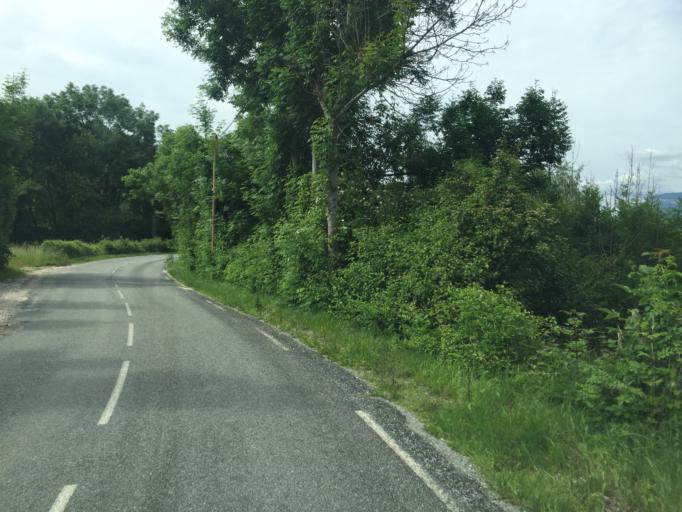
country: FR
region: Rhone-Alpes
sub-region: Departement de la Savoie
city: Jacob-Bellecombette
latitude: 45.5148
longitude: 5.9166
